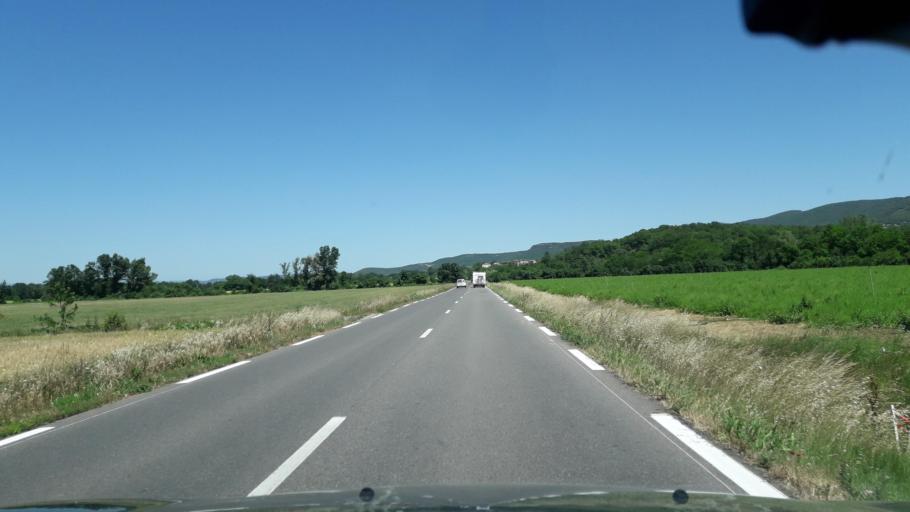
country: FR
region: Rhone-Alpes
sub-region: Departement de l'Ardeche
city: Lablachere
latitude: 44.3863
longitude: 4.2449
